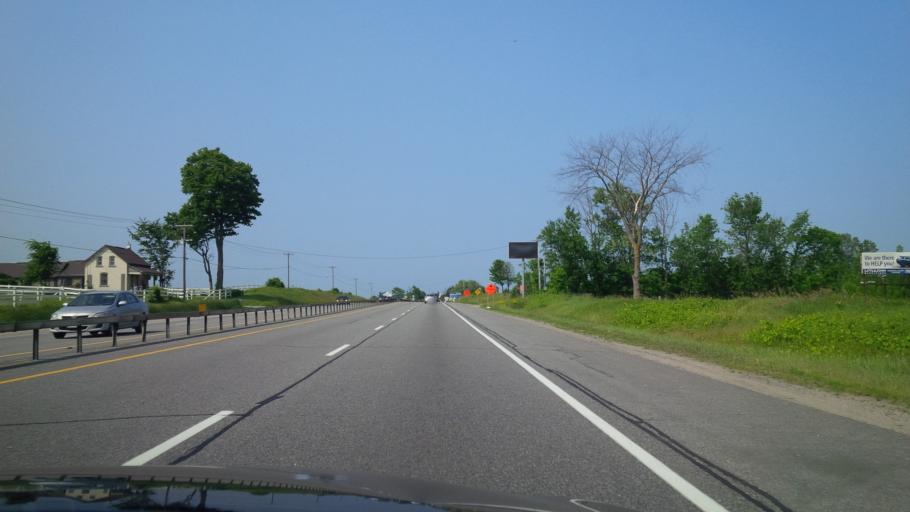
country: CA
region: Ontario
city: Barrie
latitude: 44.4412
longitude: -79.6254
